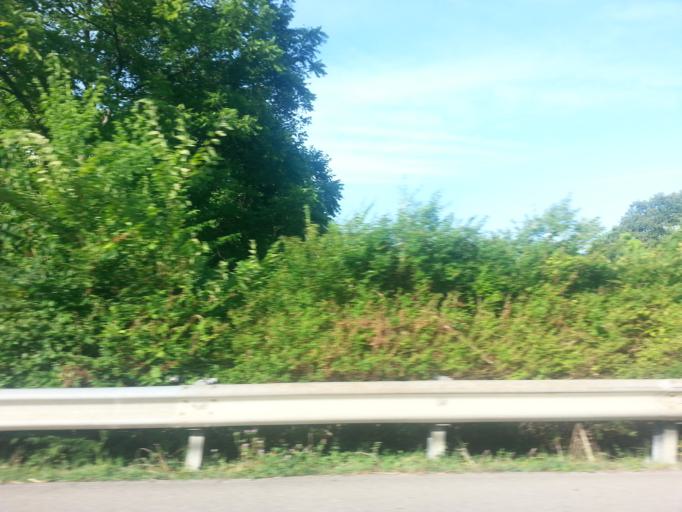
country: US
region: Tennessee
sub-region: Knox County
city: Knoxville
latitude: 35.9223
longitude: -83.9334
